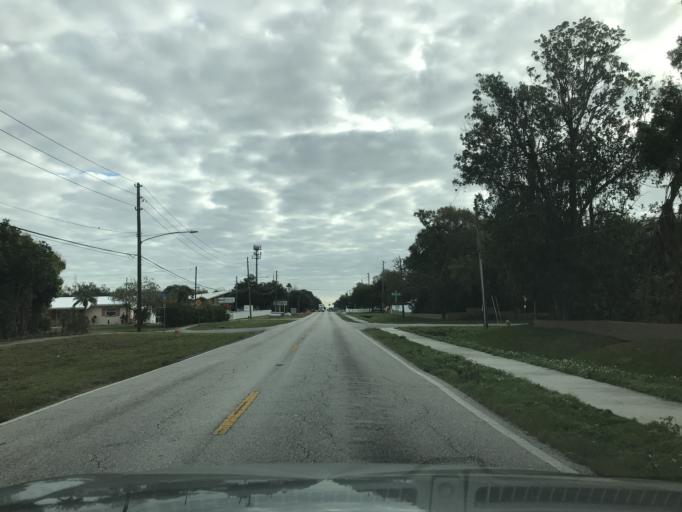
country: US
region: Florida
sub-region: Pinellas County
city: Belleair
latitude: 27.9389
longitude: -82.7792
